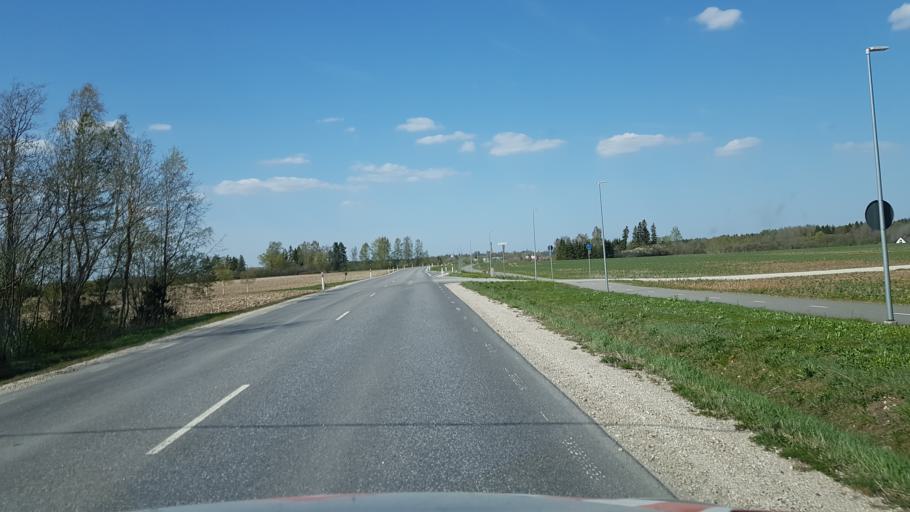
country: EE
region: Harju
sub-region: Raasiku vald
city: Arukula
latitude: 59.1902
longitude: 25.1128
